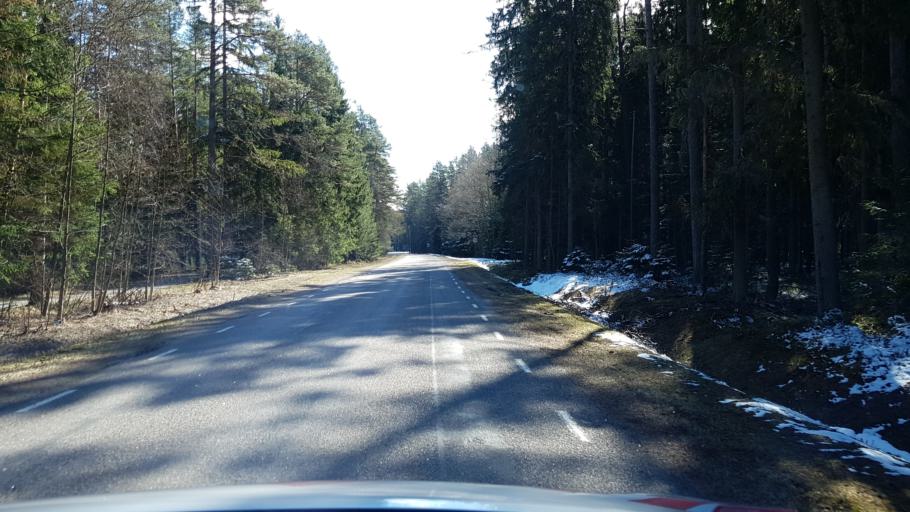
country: EE
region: Harju
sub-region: Loksa linn
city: Loksa
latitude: 59.5772
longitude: 25.9228
